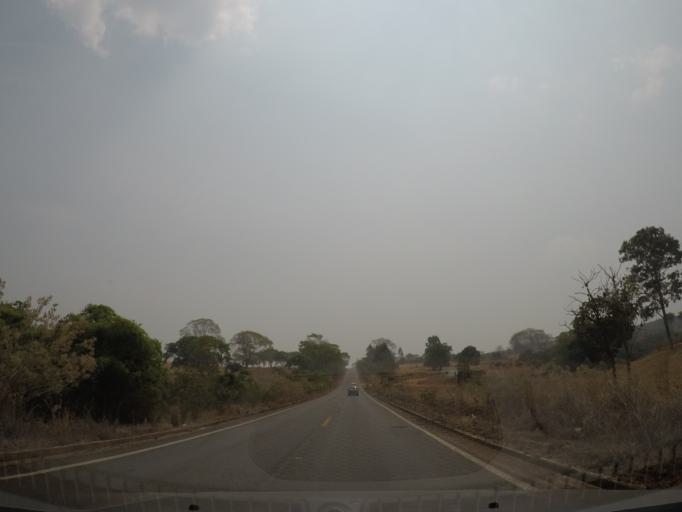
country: BR
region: Goias
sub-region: Pirenopolis
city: Pirenopolis
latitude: -15.8965
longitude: -48.8780
